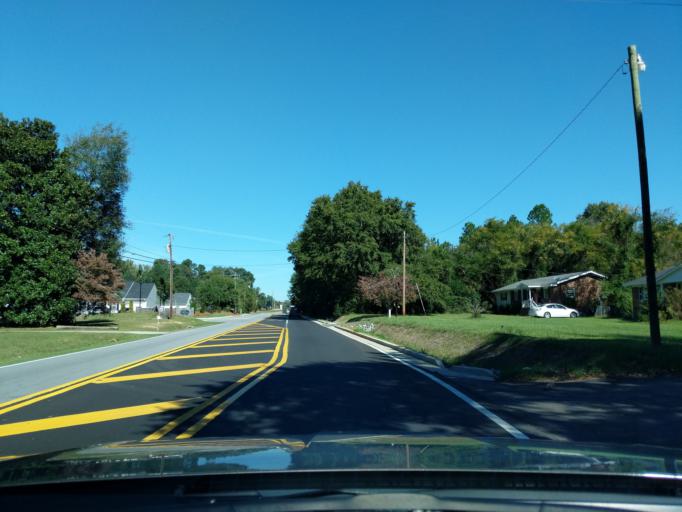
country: US
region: Georgia
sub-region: Richmond County
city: Augusta
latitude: 33.3624
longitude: -81.9969
